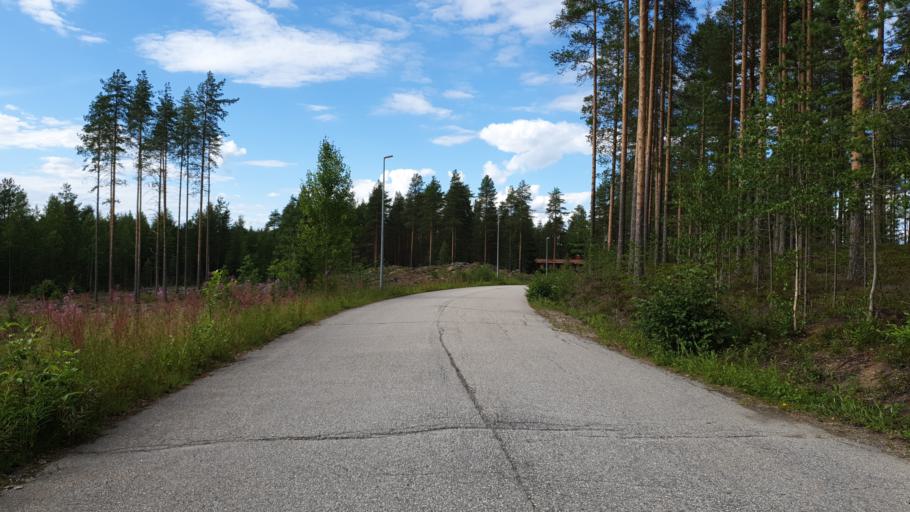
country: FI
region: Kainuu
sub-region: Kehys-Kainuu
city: Kuhmo
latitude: 64.1266
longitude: 29.5544
